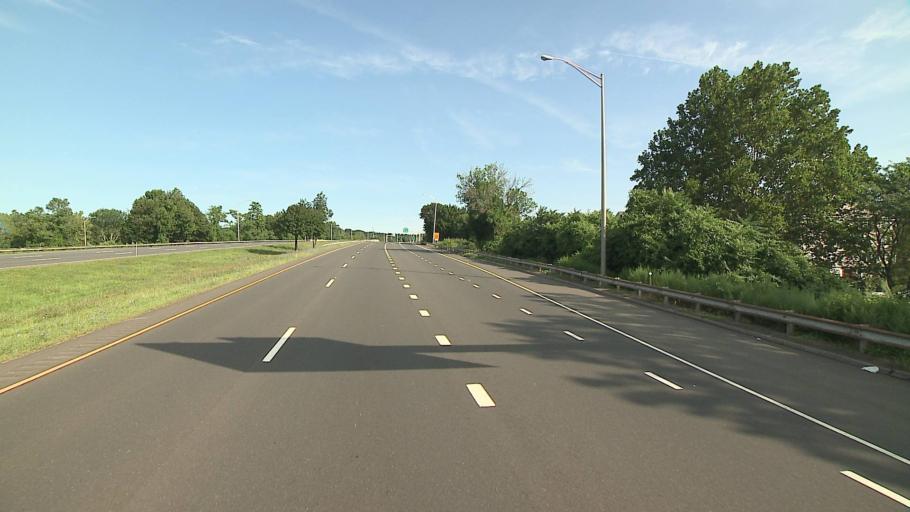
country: US
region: Connecticut
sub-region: Fairfield County
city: Norwalk
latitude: 41.1246
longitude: -73.4250
